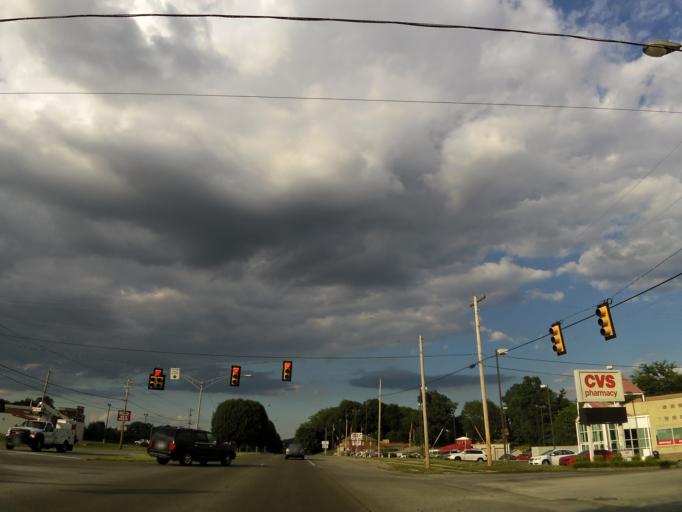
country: US
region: Tennessee
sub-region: Maury County
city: Columbia
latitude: 35.6295
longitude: -87.0255
